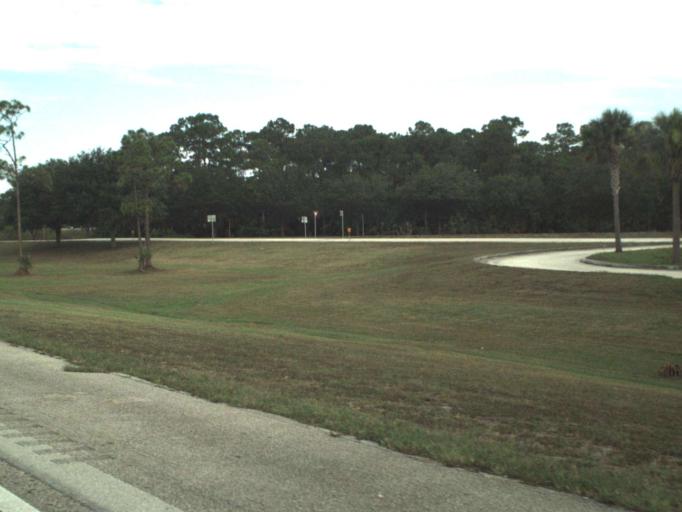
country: US
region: Florida
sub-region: Martin County
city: Palm City
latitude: 27.1275
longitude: -80.3338
